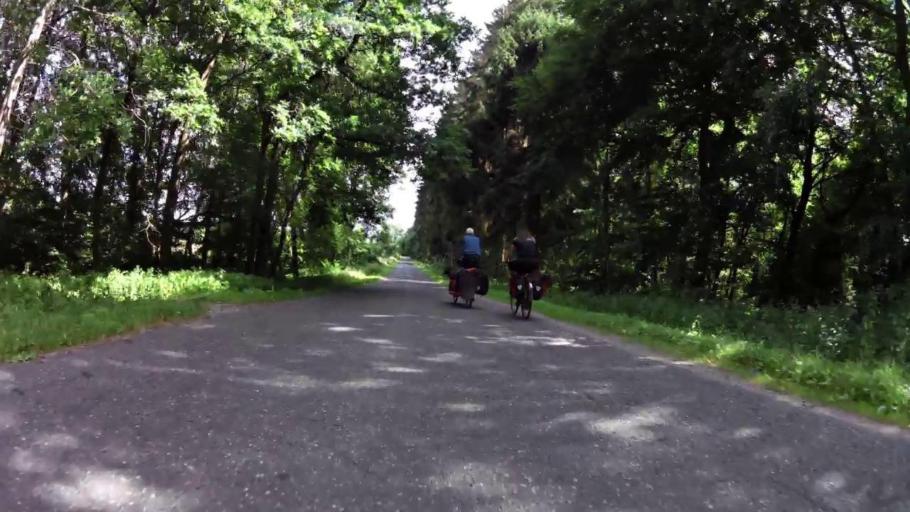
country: PL
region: West Pomeranian Voivodeship
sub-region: Powiat lobeski
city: Lobez
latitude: 53.6609
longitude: 15.5555
